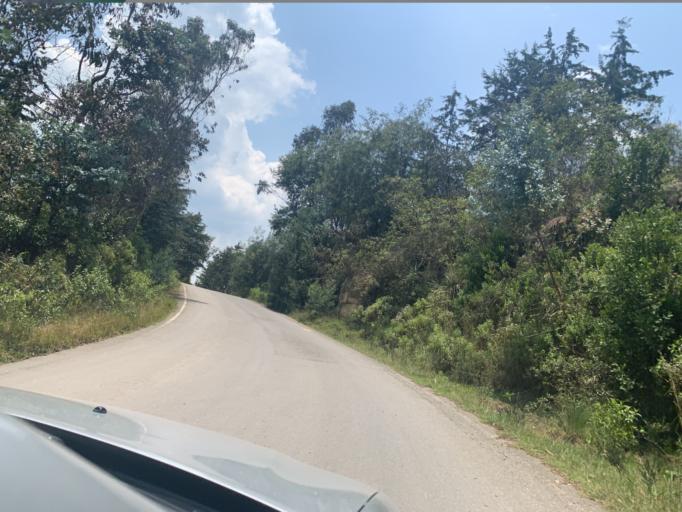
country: CO
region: Boyaca
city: Chiquinquira
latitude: 5.5785
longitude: -73.7483
